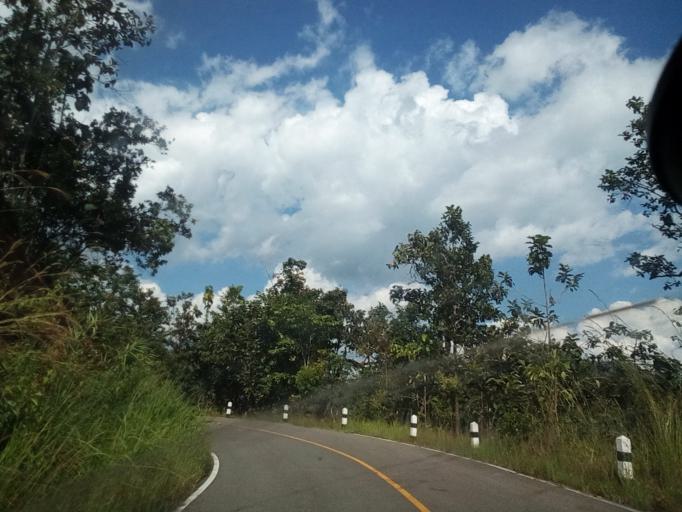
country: TH
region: Chiang Mai
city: Samoeng
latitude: 18.8724
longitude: 98.6900
